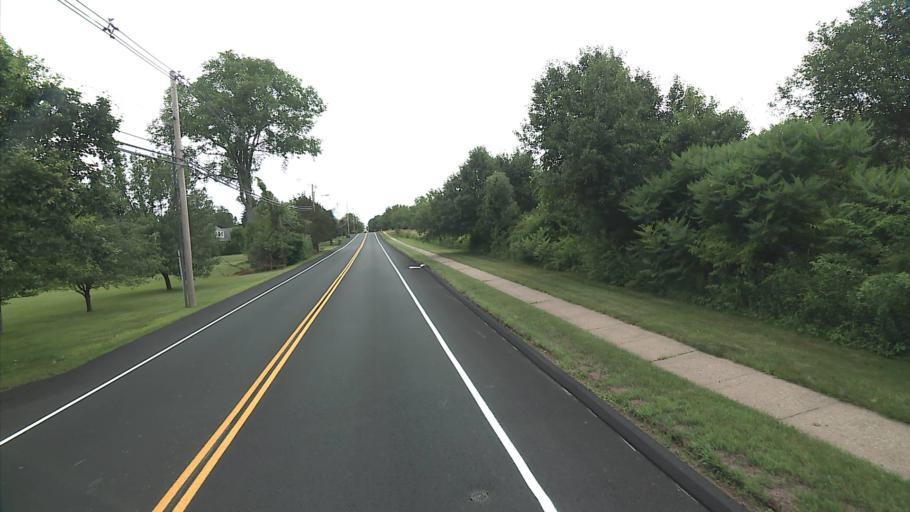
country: US
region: Connecticut
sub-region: New Haven County
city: Wallingford Center
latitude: 41.4227
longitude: -72.8022
